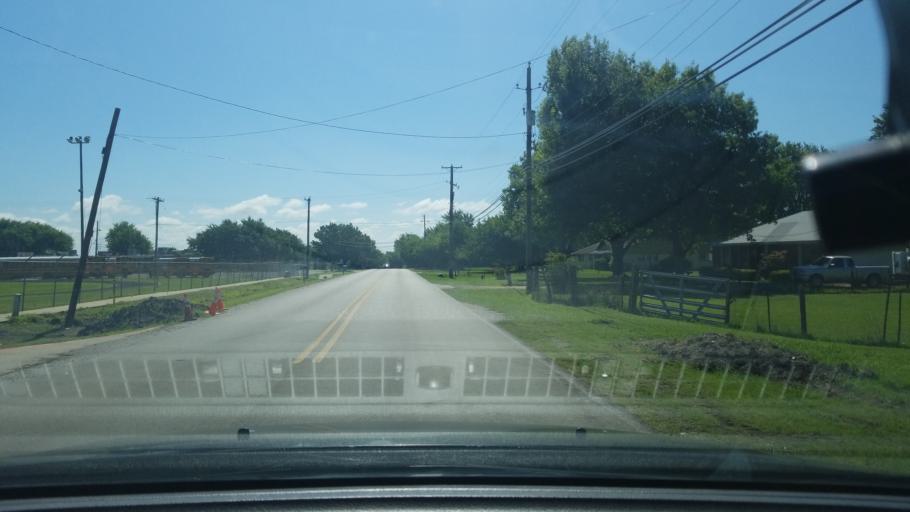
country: US
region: Texas
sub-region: Dallas County
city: Sunnyvale
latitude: 32.7945
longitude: -96.5598
